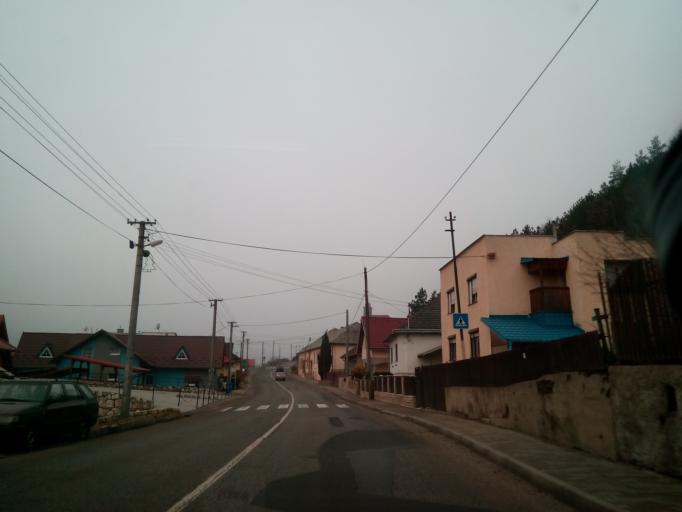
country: SK
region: Kosicky
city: Krompachy
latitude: 48.9283
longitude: 20.8532
